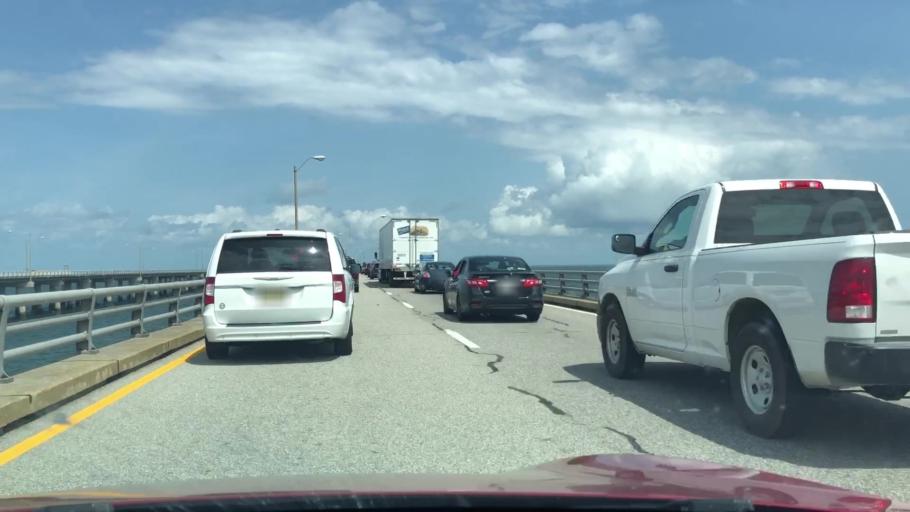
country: US
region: Virginia
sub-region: City of Virginia Beach
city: Virginia Beach
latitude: 36.9477
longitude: -76.1194
